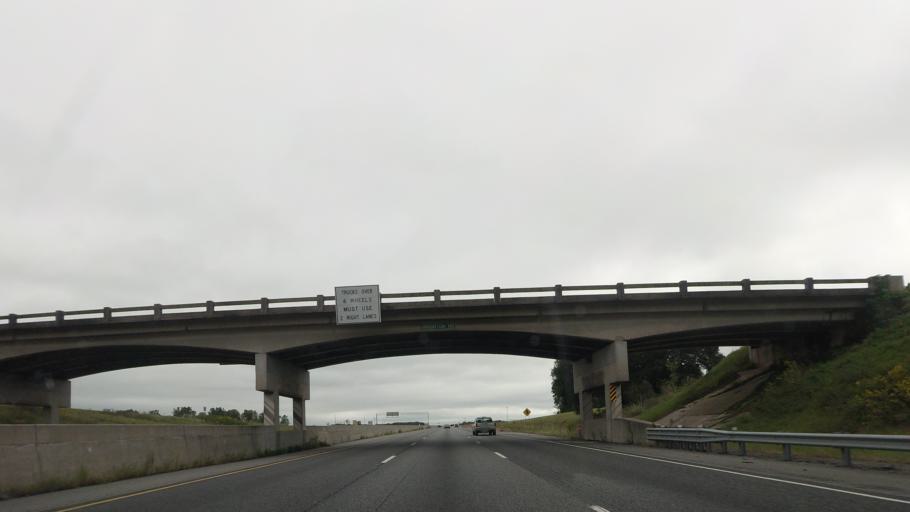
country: US
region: Georgia
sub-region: Tift County
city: Tifton
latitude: 31.5063
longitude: -83.5154
